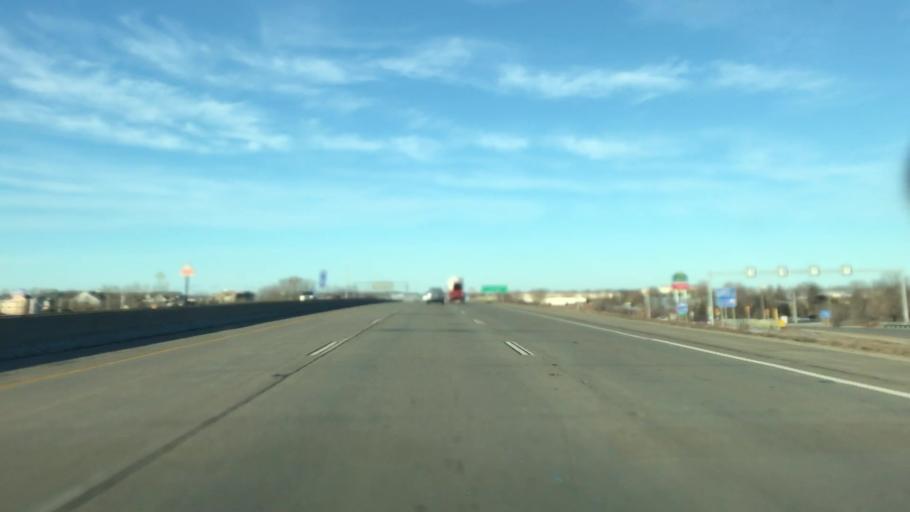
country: US
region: Wisconsin
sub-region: Outagamie County
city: Appleton
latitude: 44.2594
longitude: -88.4661
